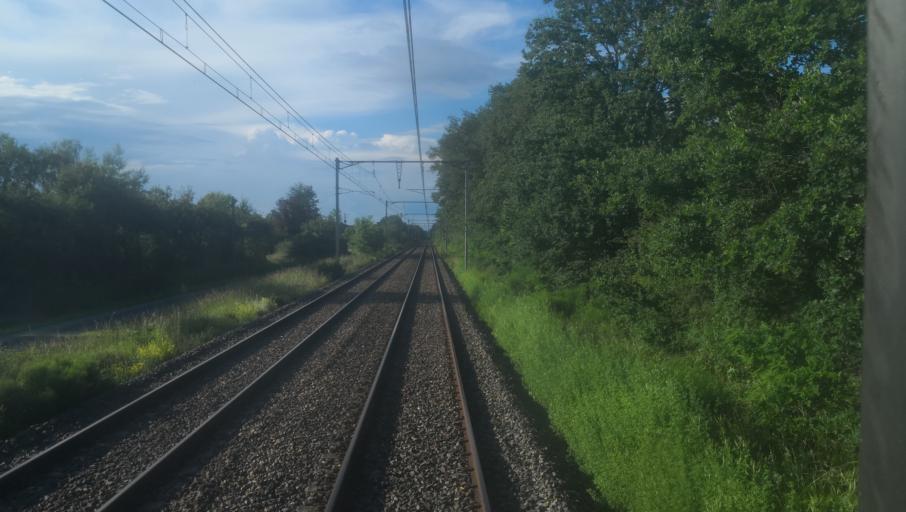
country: FR
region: Centre
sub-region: Departement du Loir-et-Cher
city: Theillay
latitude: 47.2983
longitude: 2.0430
